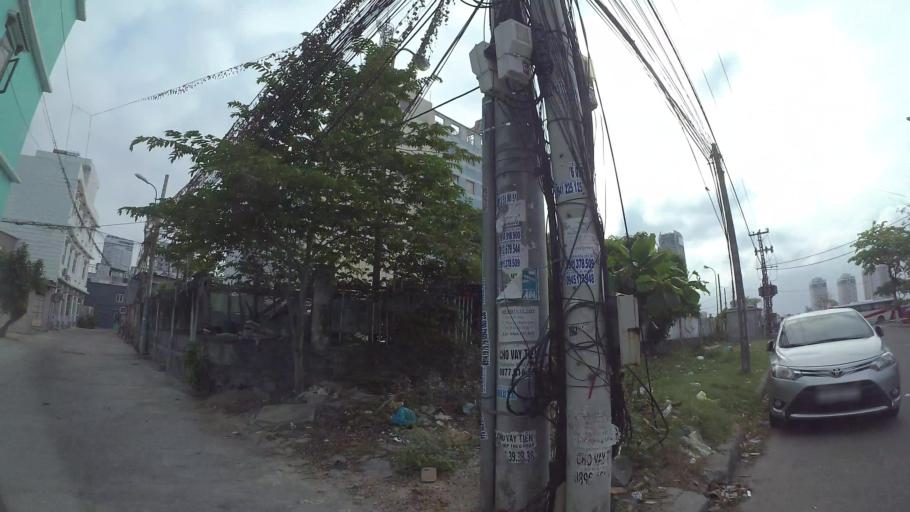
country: VN
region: Da Nang
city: Da Nang
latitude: 16.0786
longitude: 108.2295
